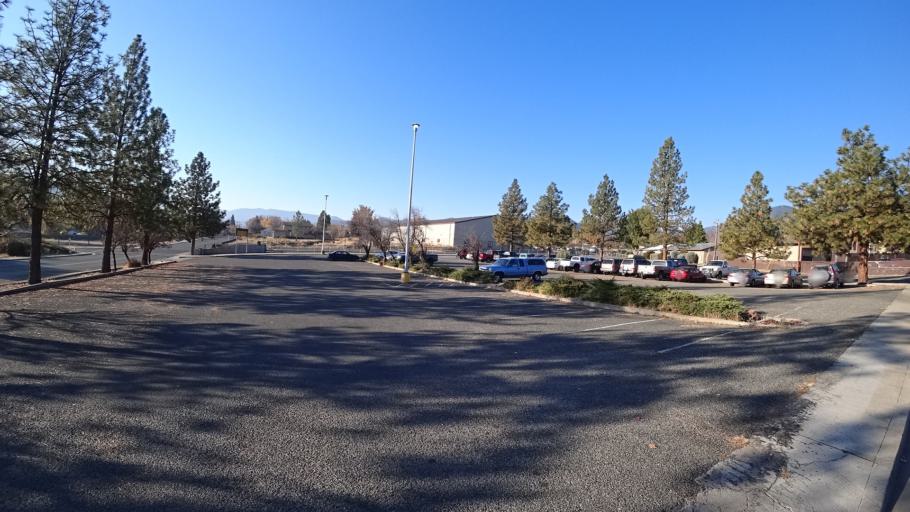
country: US
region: California
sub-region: Siskiyou County
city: Yreka
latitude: 41.7410
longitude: -122.6353
